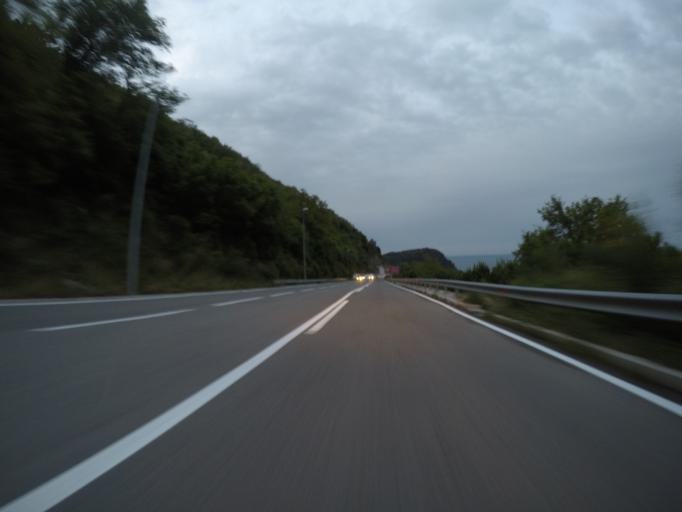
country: ME
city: Petrovac na Moru
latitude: 42.2076
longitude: 18.9491
